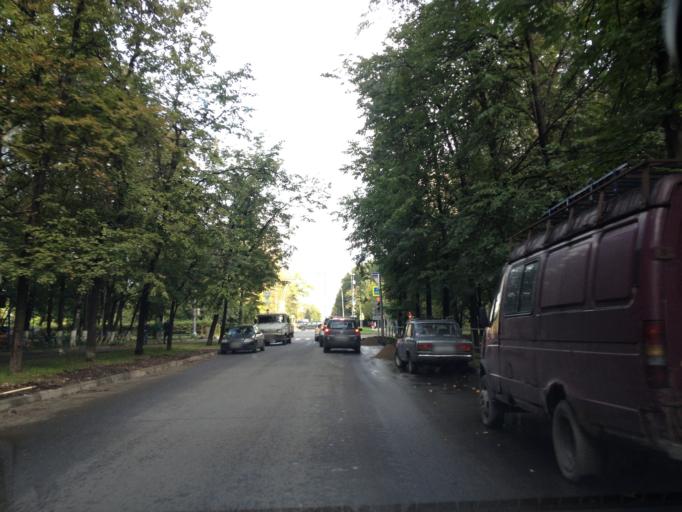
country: RU
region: Moskovskaya
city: Izmaylovo
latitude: 55.8020
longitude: 37.8051
